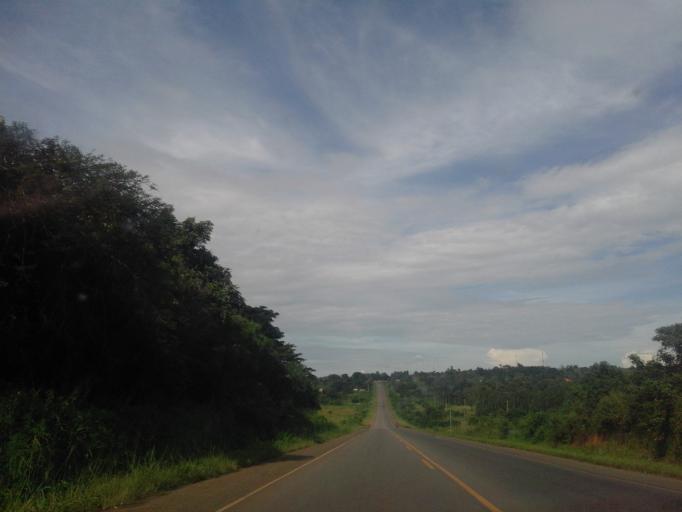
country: UG
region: Central Region
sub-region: Lwengo District
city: Lwengo
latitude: -0.3650
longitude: 31.5399
